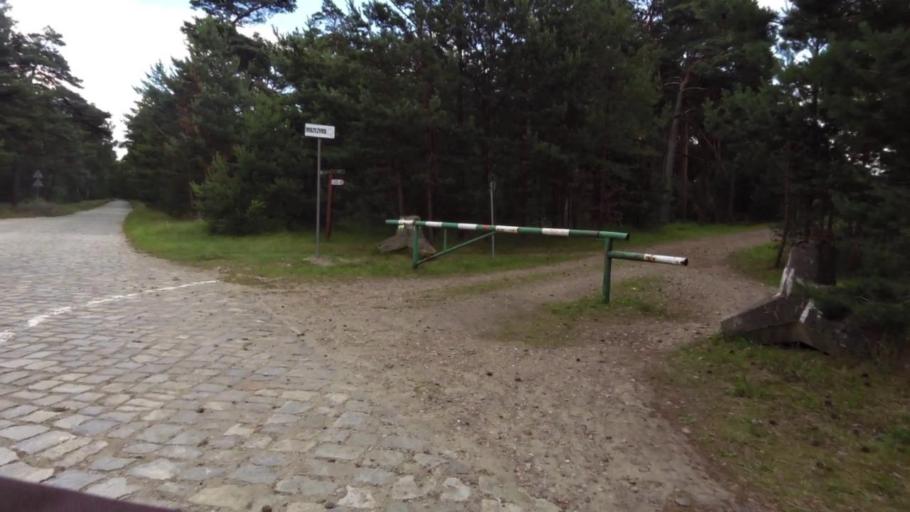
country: PL
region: West Pomeranian Voivodeship
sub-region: Powiat gryficki
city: Mrzezyno
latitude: 54.1269
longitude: 15.2204
